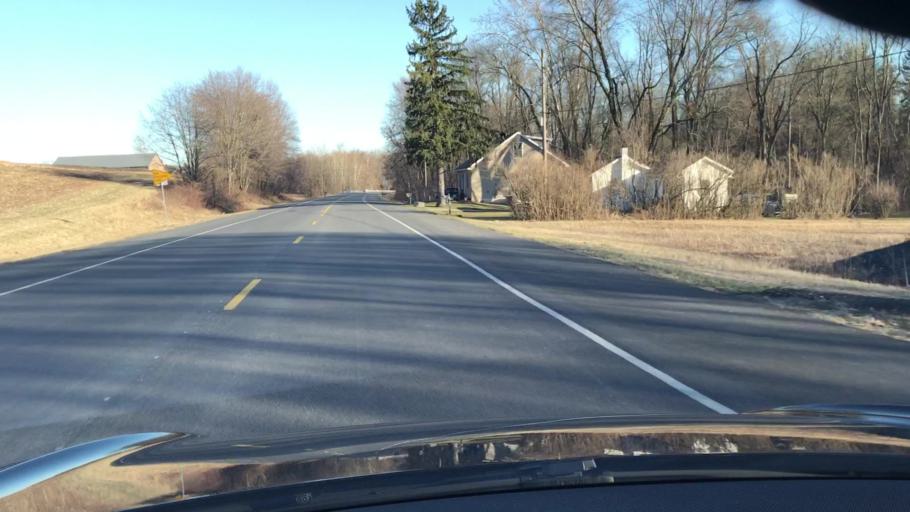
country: US
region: Pennsylvania
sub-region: York County
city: Valley Green
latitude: 40.1403
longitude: -76.8697
